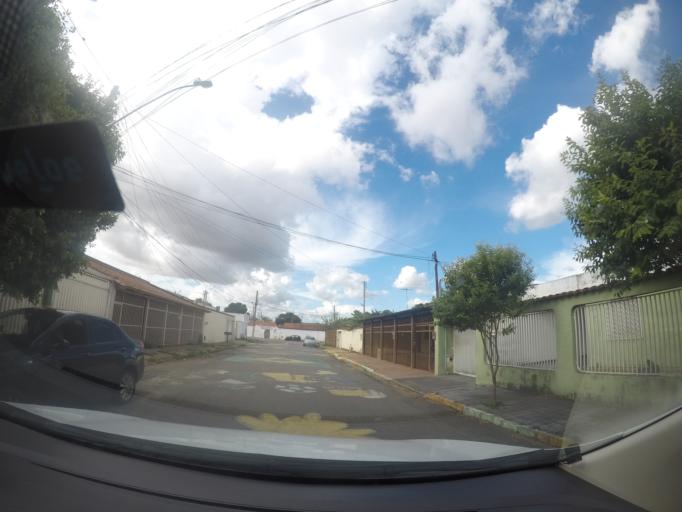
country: BR
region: Goias
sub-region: Goiania
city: Goiania
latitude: -16.6733
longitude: -49.3045
